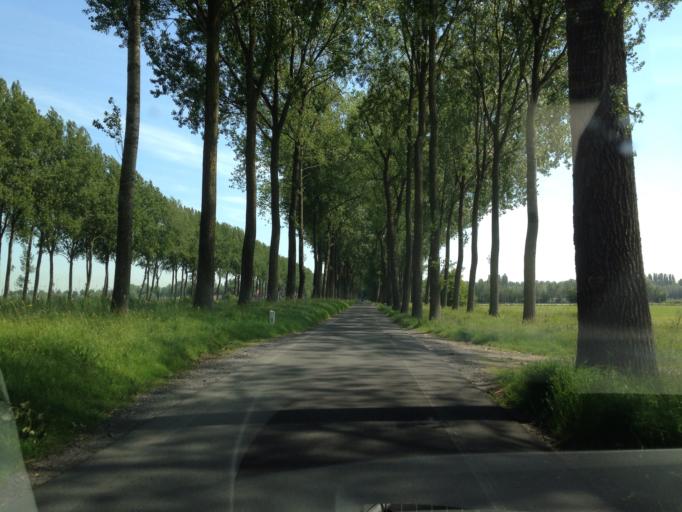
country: BE
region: Flanders
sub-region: Provincie West-Vlaanderen
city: Damme
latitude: 51.2875
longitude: 3.3295
